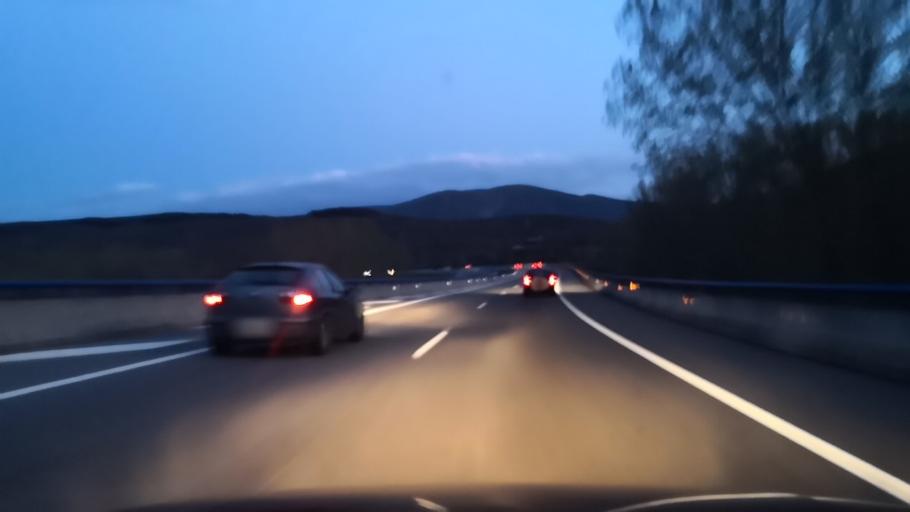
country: ES
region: Castille and Leon
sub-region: Provincia de Leon
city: Torre del Bierzo
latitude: 42.6087
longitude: -6.3866
